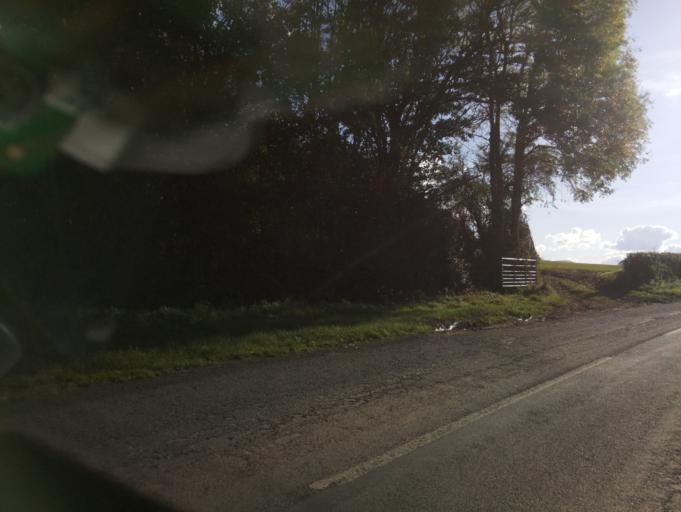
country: GB
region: England
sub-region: Herefordshire
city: Clifford
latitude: 52.0966
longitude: -3.1084
